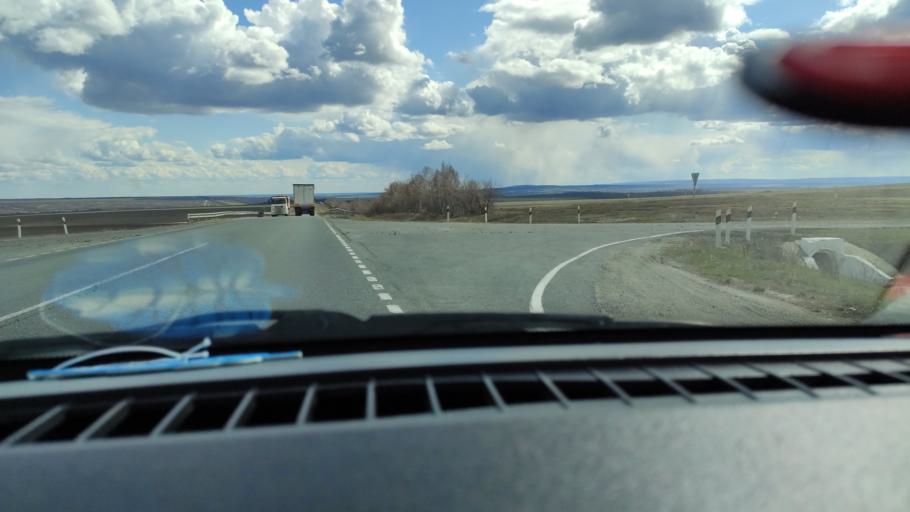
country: RU
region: Saratov
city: Dukhovnitskoye
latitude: 52.7861
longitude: 48.2331
